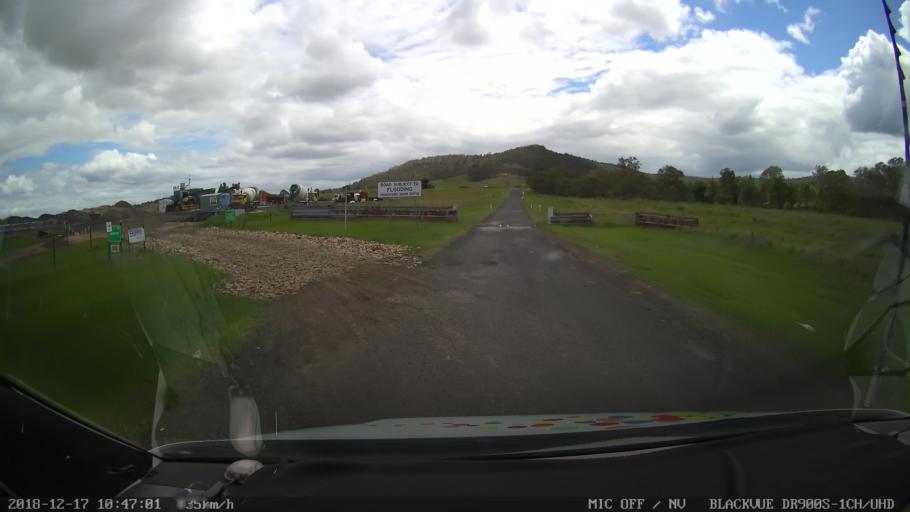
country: AU
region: New South Wales
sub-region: Clarence Valley
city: Gordon
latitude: -28.8826
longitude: 152.5694
